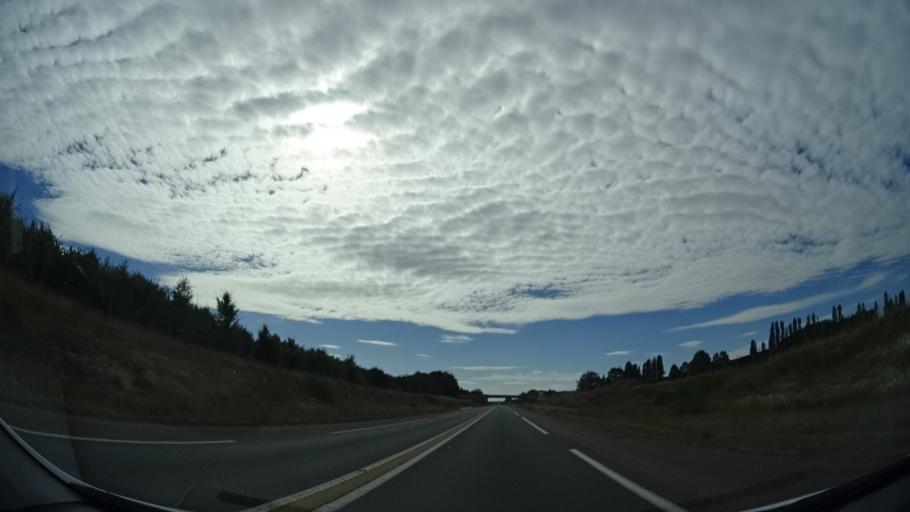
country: FR
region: Centre
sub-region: Departement du Loiret
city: Bellegarde
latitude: 47.9743
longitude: 2.4593
